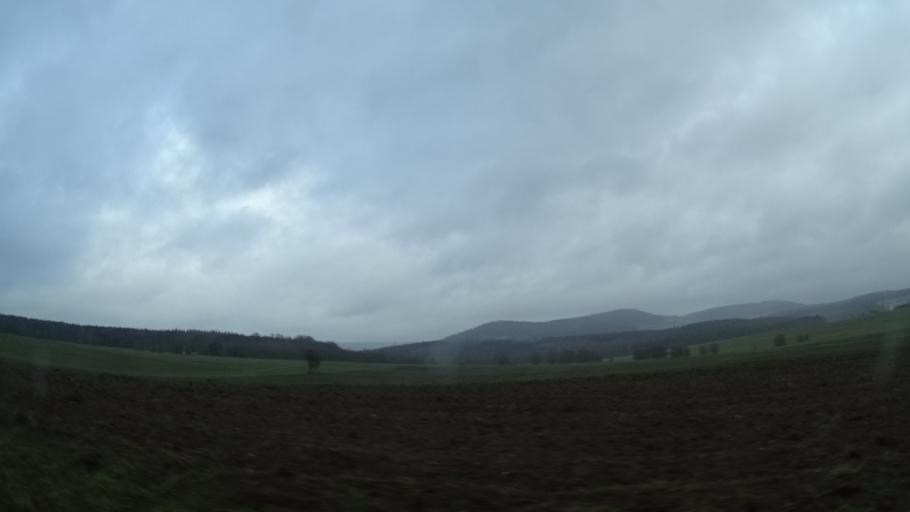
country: DE
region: Thuringia
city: Wolfershausen
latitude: 50.4732
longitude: 10.4244
